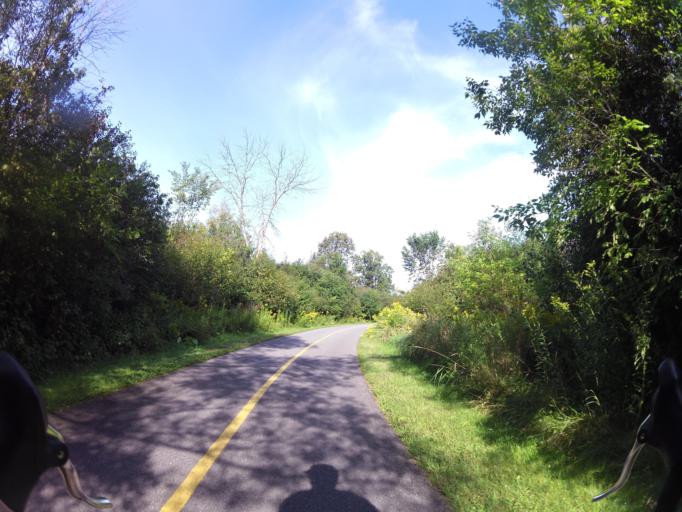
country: CA
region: Ontario
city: Bells Corners
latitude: 45.3418
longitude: -75.8741
